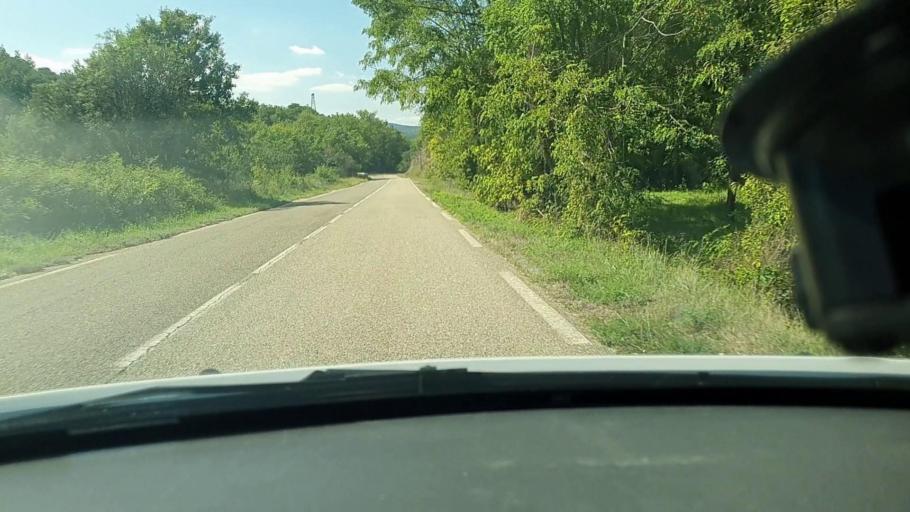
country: FR
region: Languedoc-Roussillon
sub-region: Departement du Gard
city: Sabran
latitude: 44.2188
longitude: 4.5381
